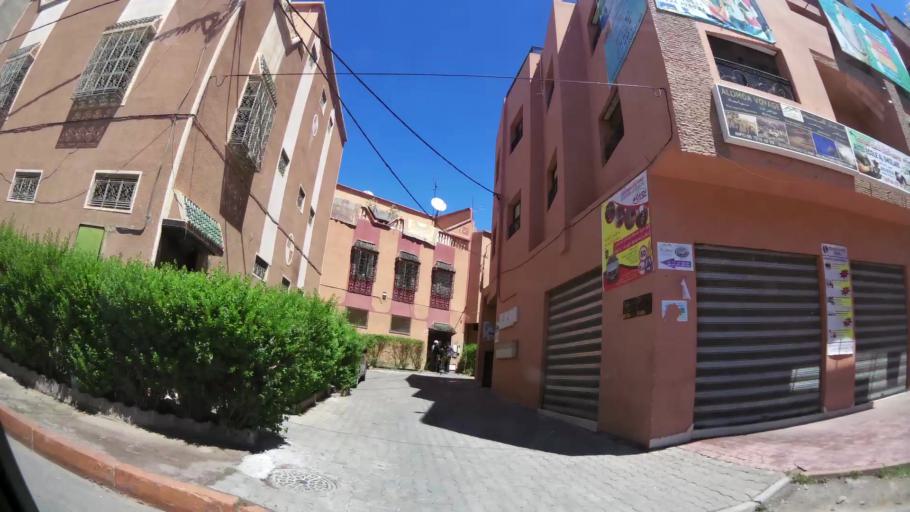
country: MA
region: Marrakech-Tensift-Al Haouz
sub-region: Marrakech
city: Marrakesh
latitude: 31.6464
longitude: -7.9931
